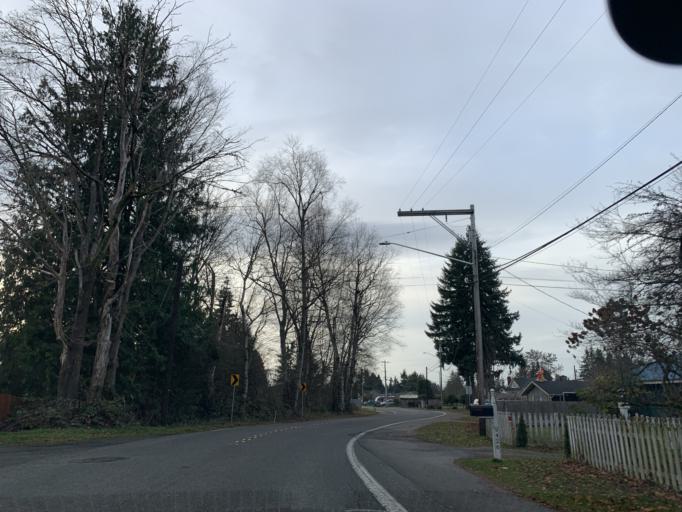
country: US
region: Washington
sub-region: Snohomish County
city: Marysville
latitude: 48.0812
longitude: -122.1565
